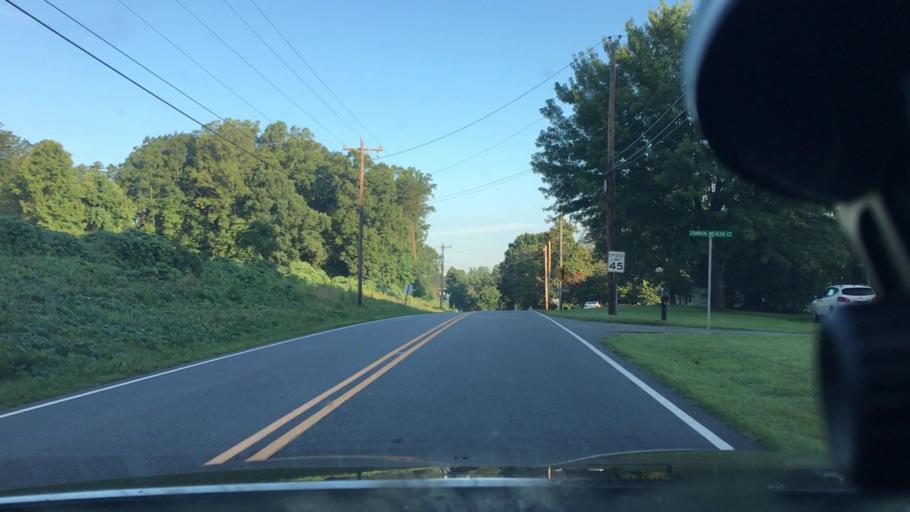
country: US
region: North Carolina
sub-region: Rutherford County
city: Rutherfordton
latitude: 35.3926
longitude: -81.9834
